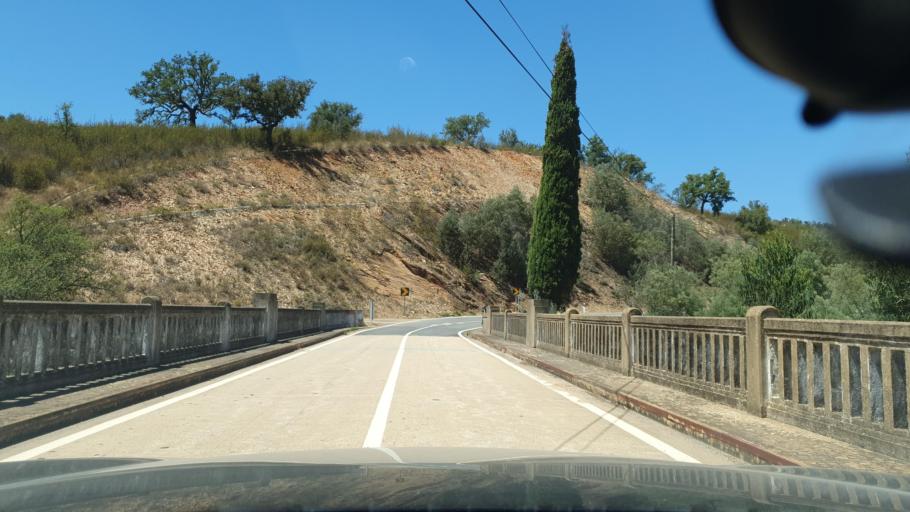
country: PT
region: Beja
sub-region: Odemira
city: Odemira
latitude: 37.5387
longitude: -8.4849
